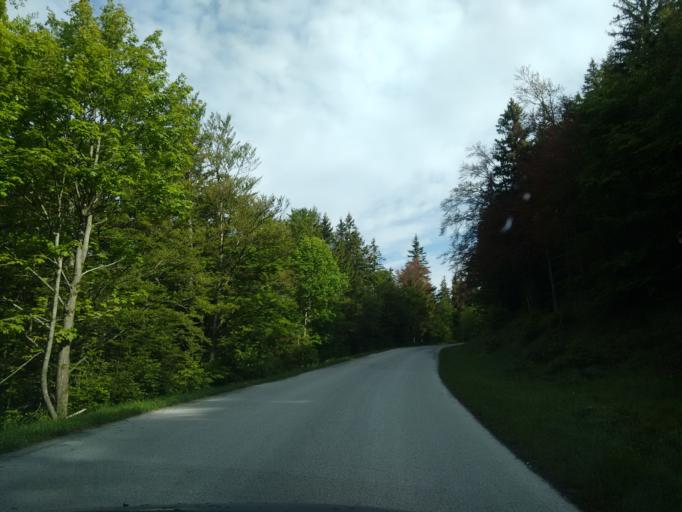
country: AT
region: Styria
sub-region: Politischer Bezirk Liezen
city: Altaussee
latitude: 47.6537
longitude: 13.7561
